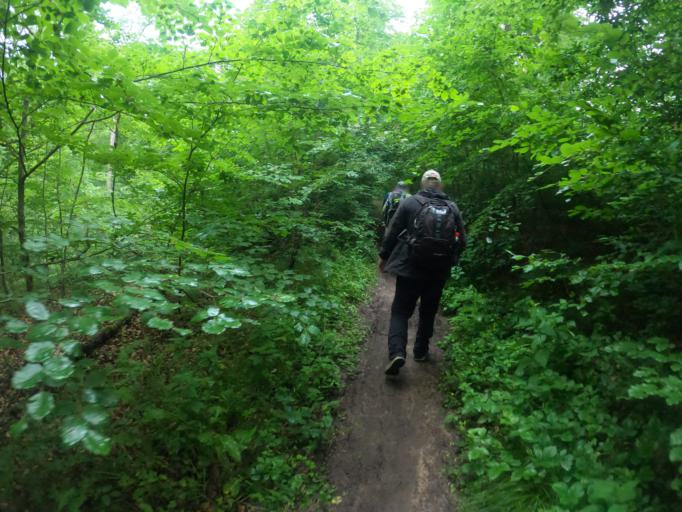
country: DE
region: Bavaria
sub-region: Upper Franconia
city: Memmelsdorf
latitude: 49.9253
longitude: 10.9711
